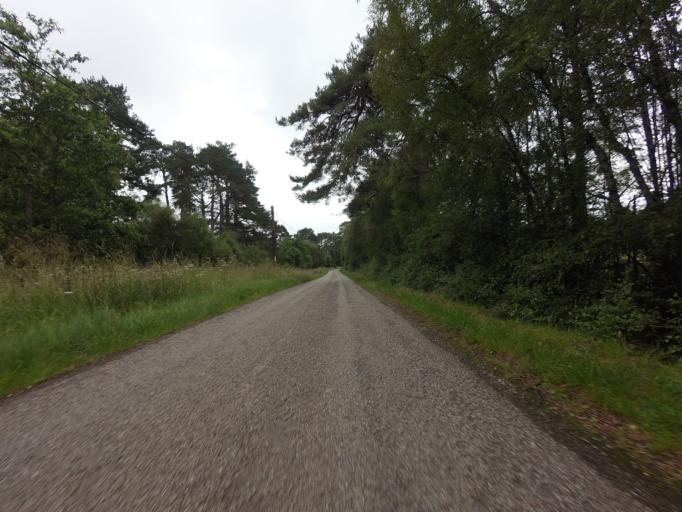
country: GB
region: Scotland
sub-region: Highland
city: Alness
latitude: 57.9897
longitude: -4.4114
